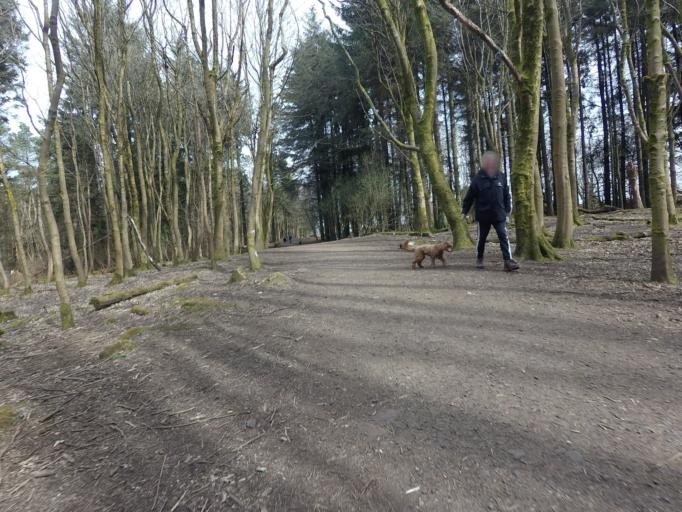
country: GB
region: Scotland
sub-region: West Lothian
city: Livingston
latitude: 55.9133
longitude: -3.5499
